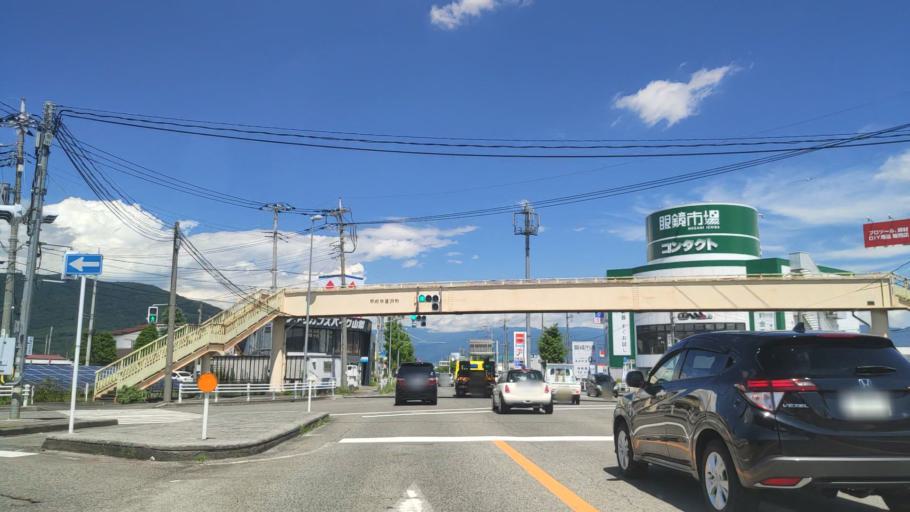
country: JP
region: Yamanashi
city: Kofu-shi
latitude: 35.6413
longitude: 138.5950
